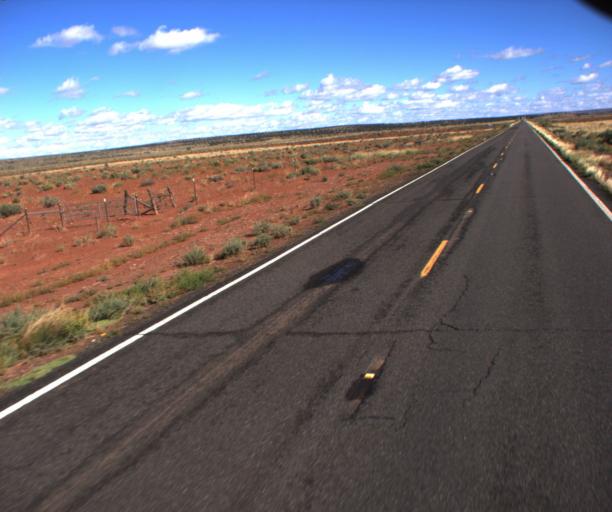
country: US
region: Arizona
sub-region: Apache County
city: Saint Johns
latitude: 34.6996
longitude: -109.2716
